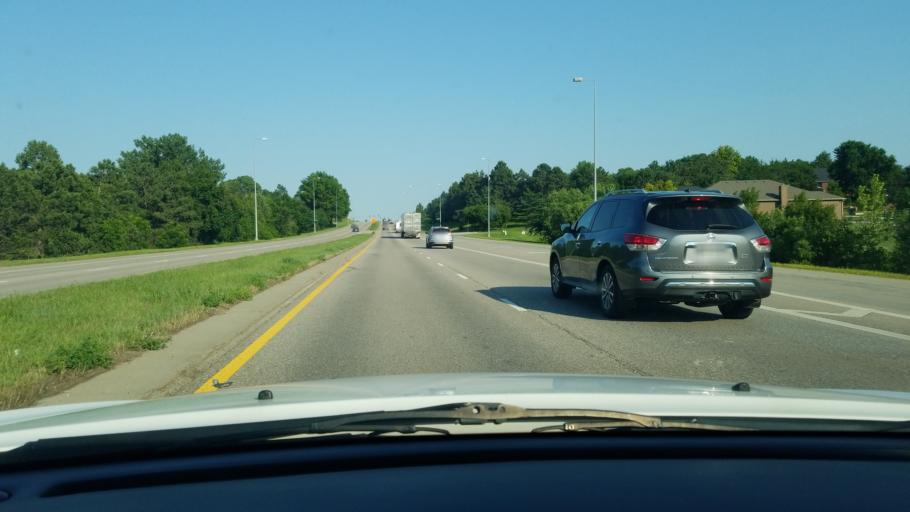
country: US
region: Nebraska
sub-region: Lancaster County
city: Lincoln
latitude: 40.7494
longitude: -96.6314
